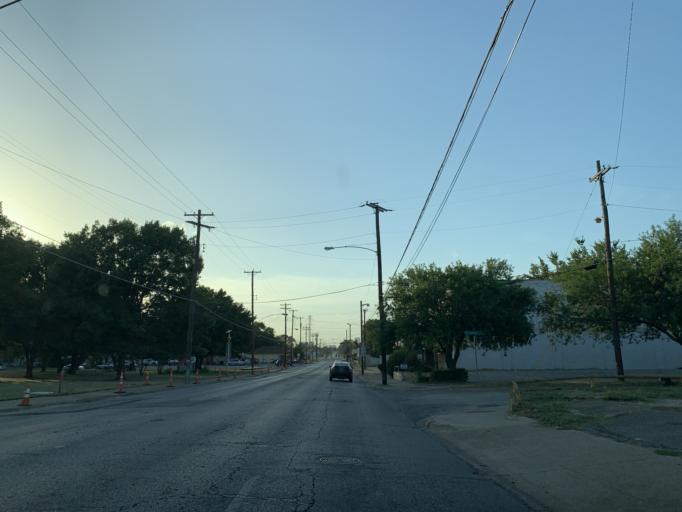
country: US
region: Texas
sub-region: Dallas County
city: Dallas
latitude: 32.7643
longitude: -96.7484
